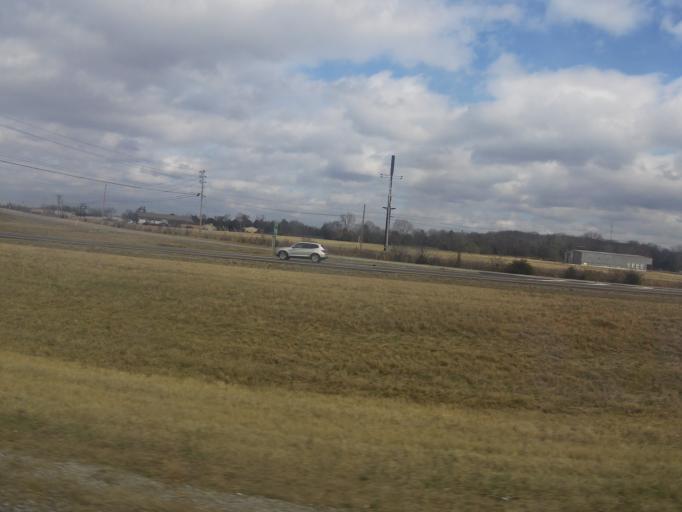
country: US
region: Tennessee
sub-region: Rutherford County
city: Plainview
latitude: 35.7208
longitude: -86.3199
